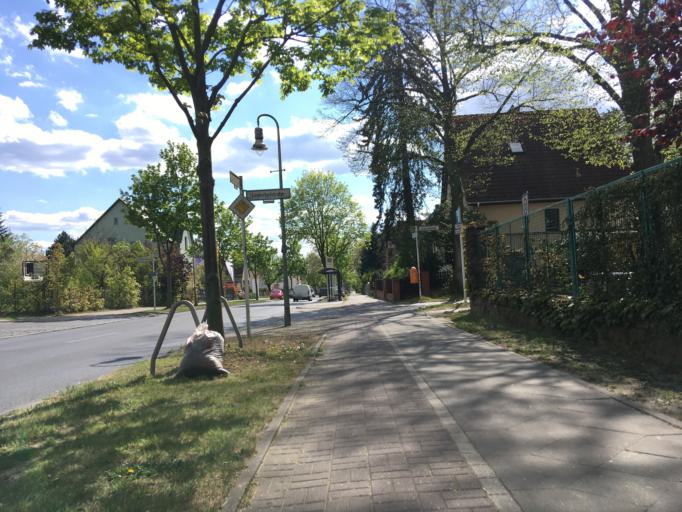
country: DE
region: Berlin
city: Mahlsdorf
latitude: 52.5176
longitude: 13.6148
